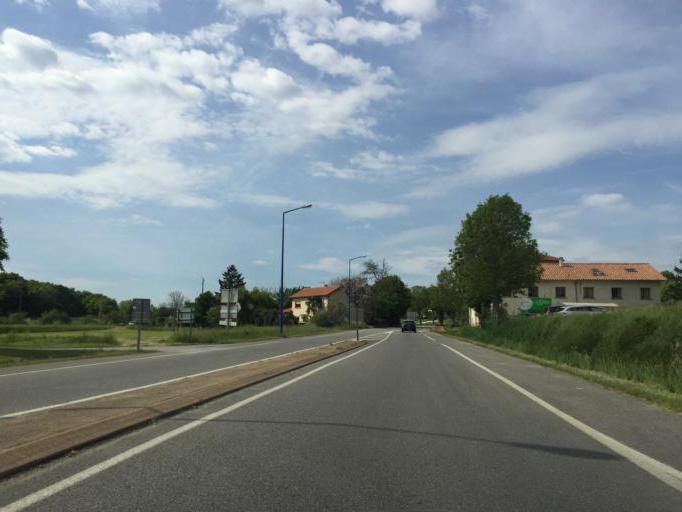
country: FR
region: Rhone-Alpes
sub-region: Departement de la Drome
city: Eurre
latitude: 44.7742
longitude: 5.0225
